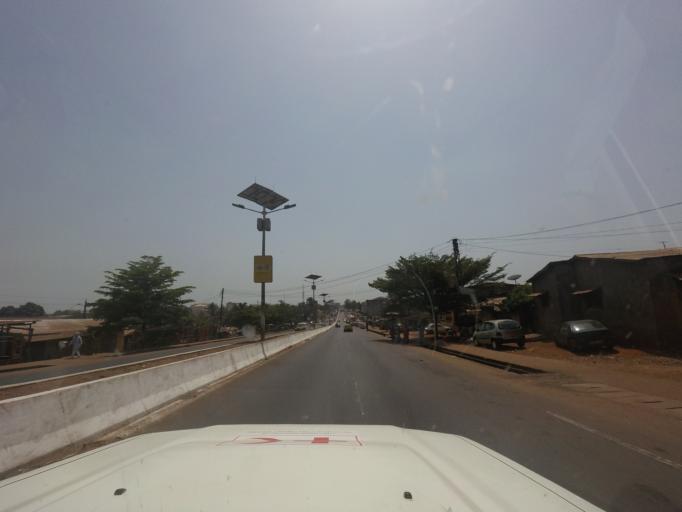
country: GN
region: Conakry
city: Conakry
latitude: 9.5641
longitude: -13.6381
